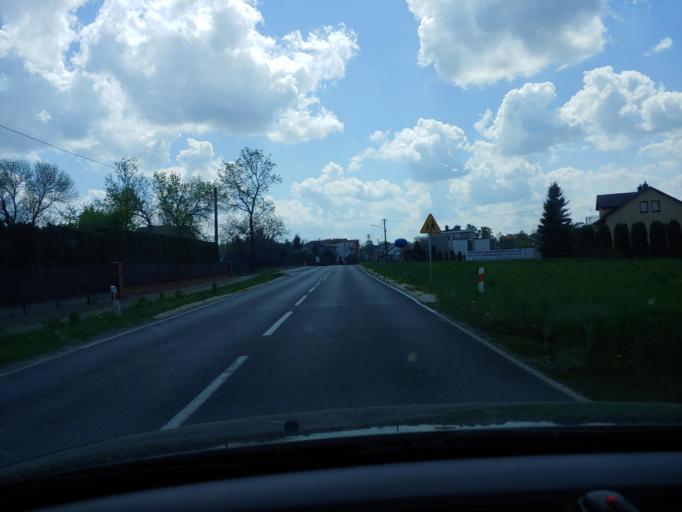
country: PL
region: Subcarpathian Voivodeship
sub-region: Powiat mielecki
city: Radomysl Wielki
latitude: 50.2007
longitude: 21.2796
